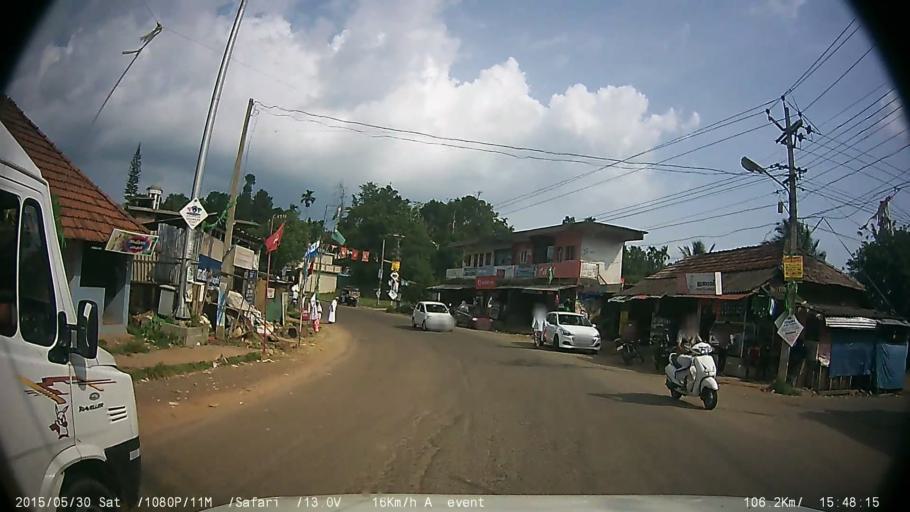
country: IN
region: Kerala
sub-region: Wayanad
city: Panamaram
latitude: 11.6996
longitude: 76.0774
